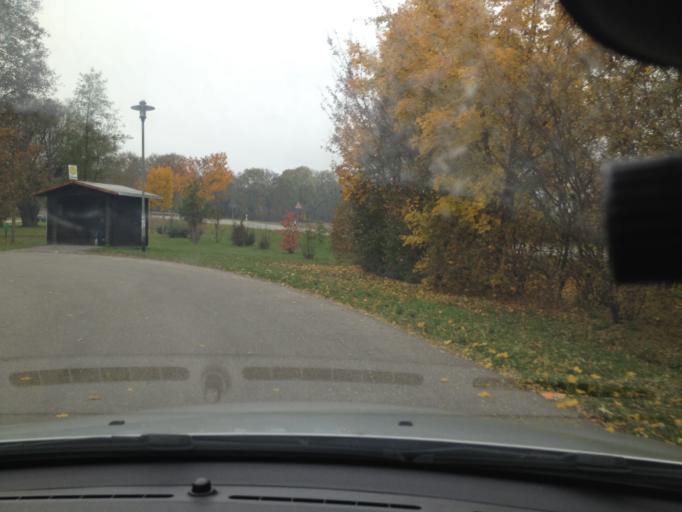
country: DE
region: Bavaria
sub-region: Swabia
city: Hiltenfingen
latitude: 48.1758
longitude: 10.7340
